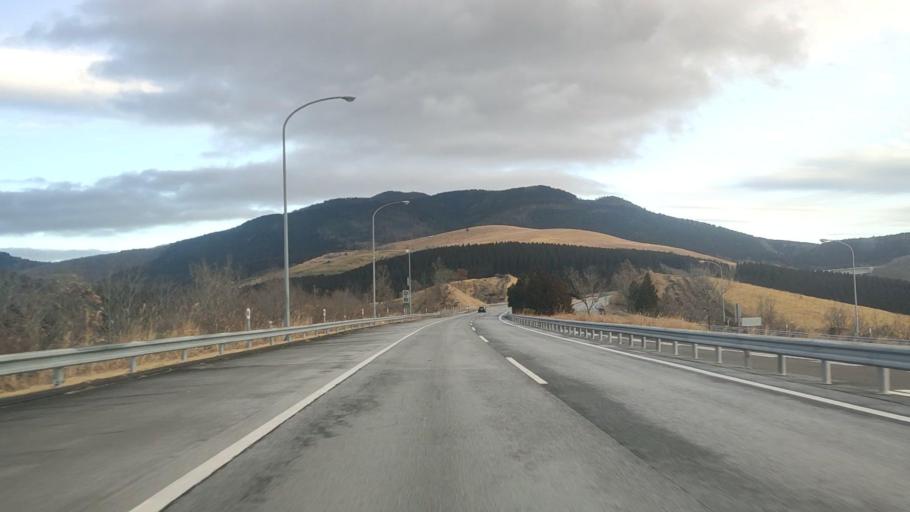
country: JP
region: Oita
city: Beppu
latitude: 33.2819
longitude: 131.3452
